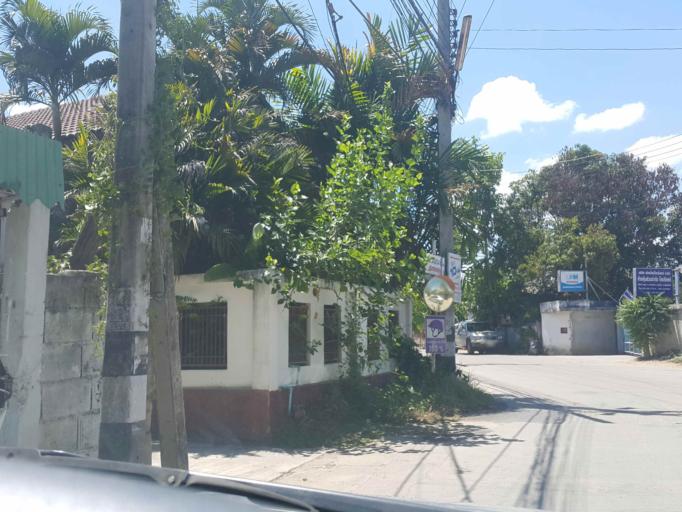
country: TH
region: Chiang Mai
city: Saraphi
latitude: 18.7616
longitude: 99.0327
